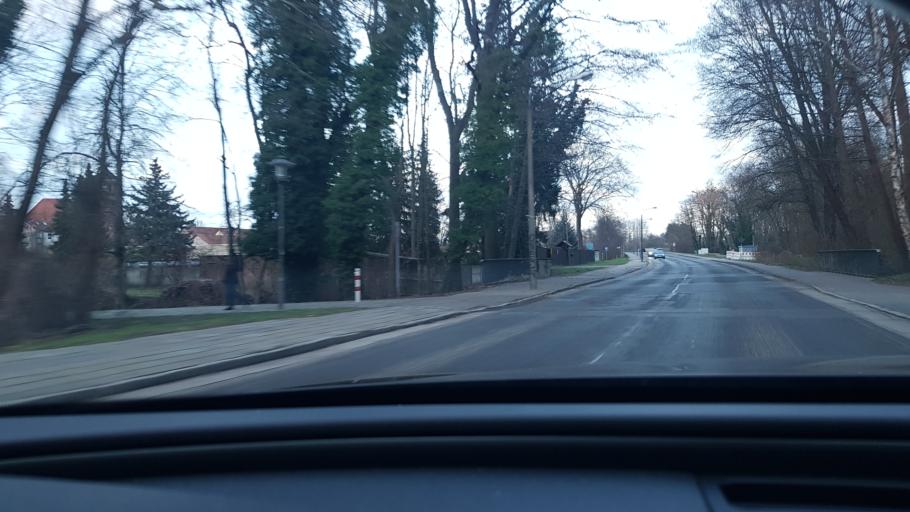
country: DE
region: Brandenburg
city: Storkow
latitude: 52.2550
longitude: 13.9341
